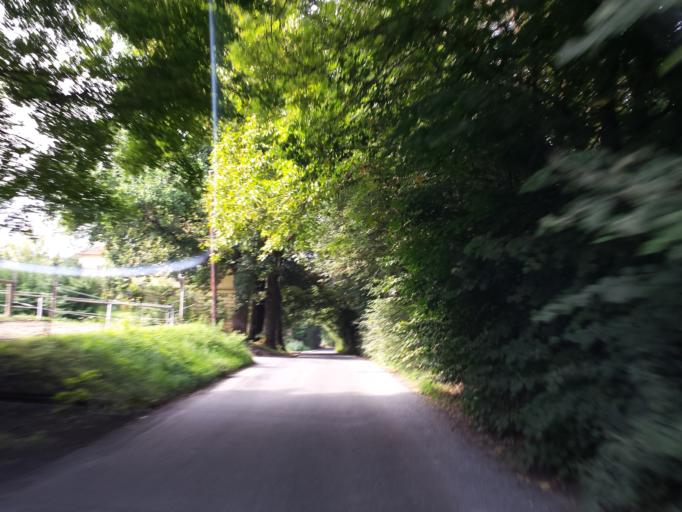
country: AT
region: Styria
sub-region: Politischer Bezirk Deutschlandsberg
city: Deutschlandsberg
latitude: 46.8137
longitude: 15.2433
